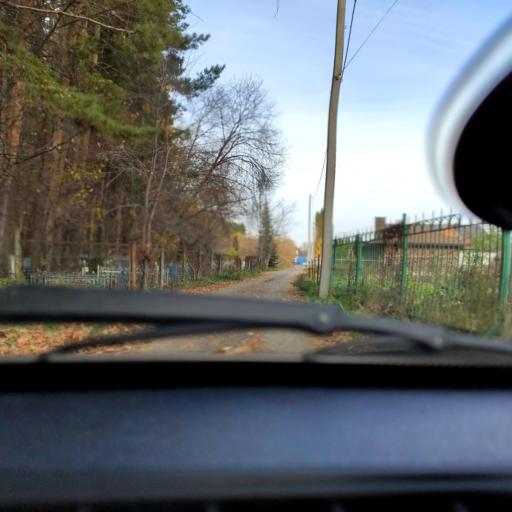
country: RU
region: Bashkortostan
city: Mikhaylovka
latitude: 54.7899
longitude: 55.9413
